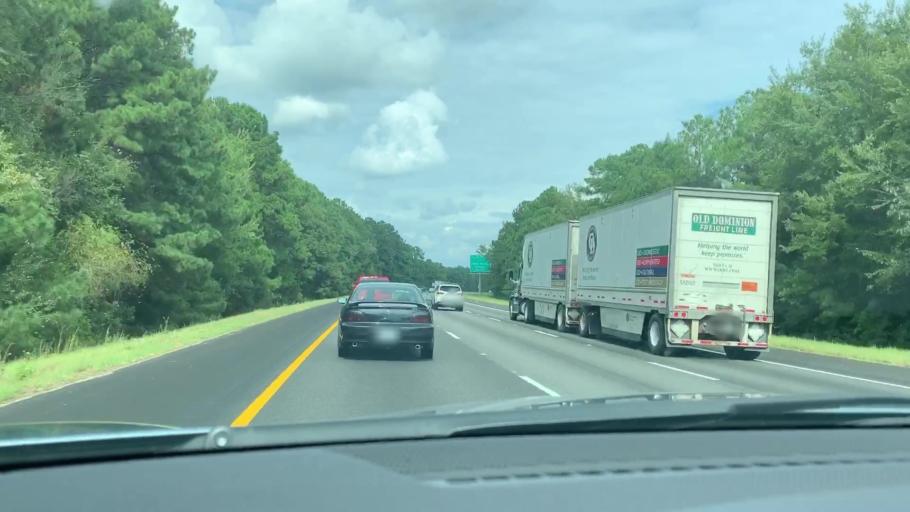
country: US
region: Georgia
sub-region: Chatham County
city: Pooler
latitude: 32.1529
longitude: -81.2369
